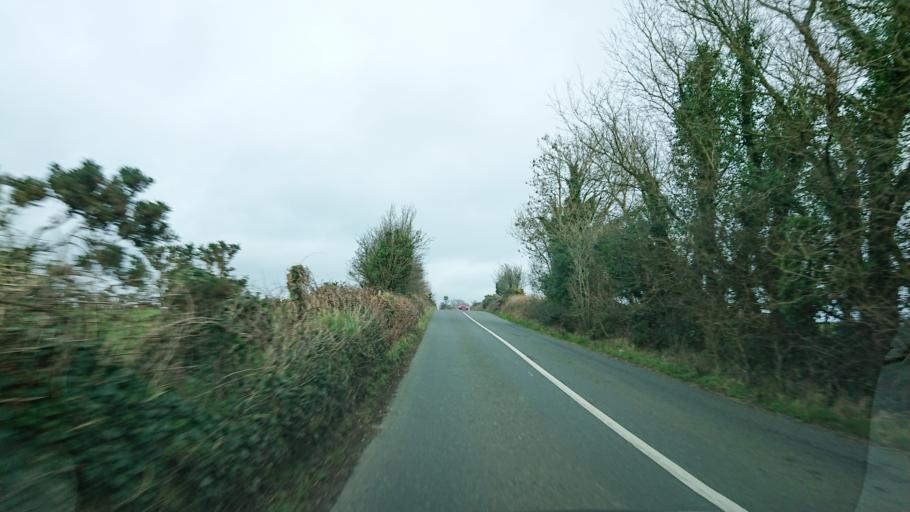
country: IE
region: Munster
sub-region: Waterford
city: Portlaw
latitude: 52.1902
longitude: -7.2845
